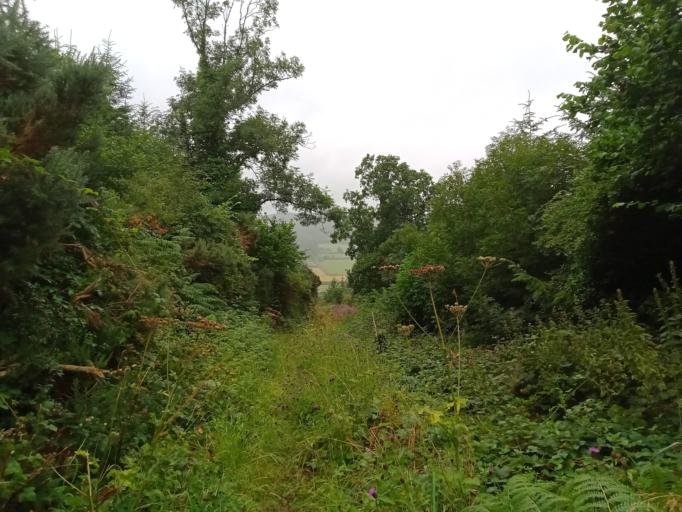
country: IE
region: Leinster
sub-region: Kilkenny
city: Ballyragget
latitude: 52.8138
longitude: -7.4304
